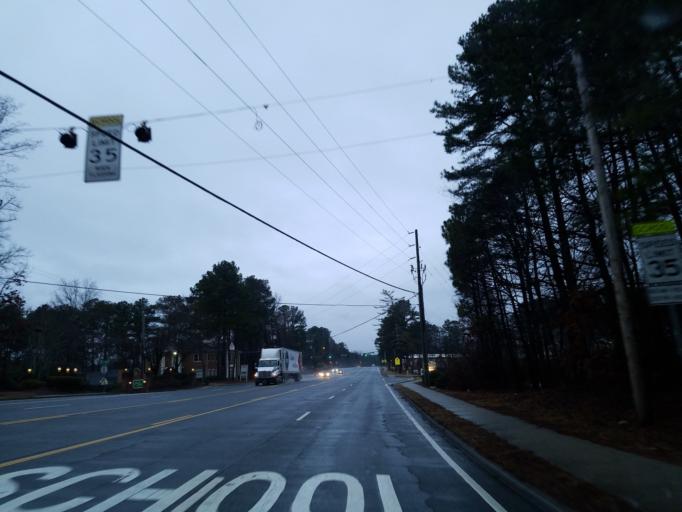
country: US
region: Georgia
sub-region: DeKalb County
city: Dunwoody
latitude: 33.9926
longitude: -84.2799
